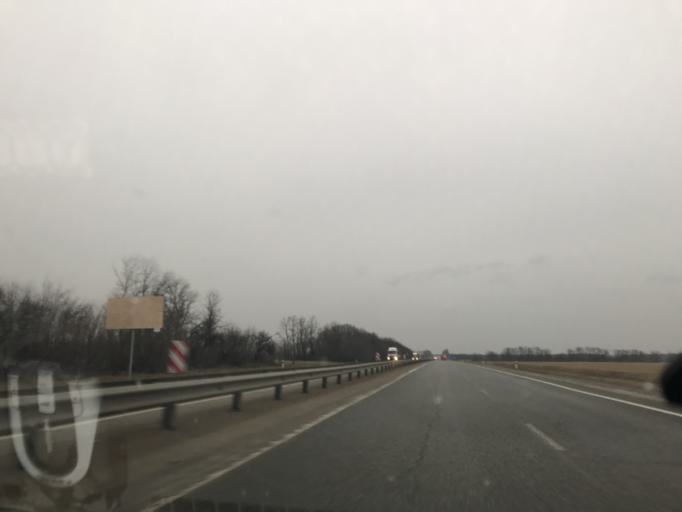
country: RU
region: Krasnodarskiy
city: Pavlovskaya
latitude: 46.2142
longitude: 39.8315
